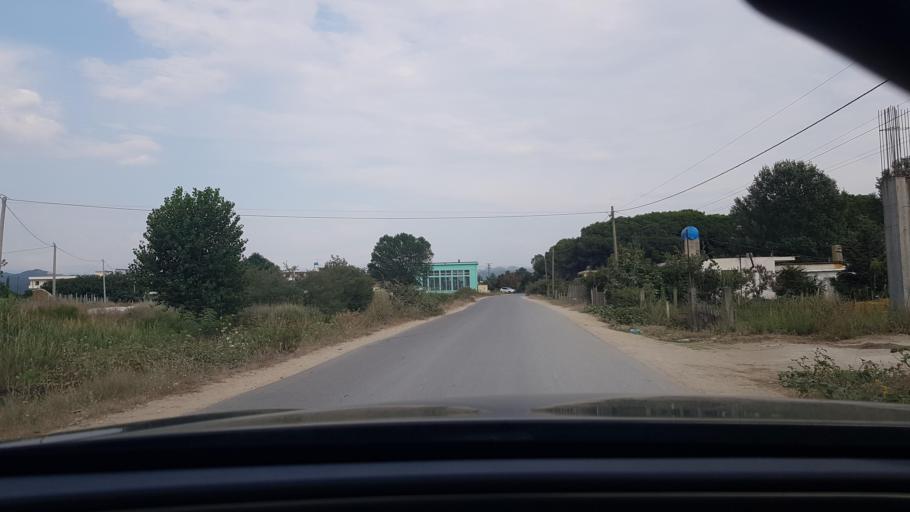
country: AL
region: Durres
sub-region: Rrethi i Durresit
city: Katundi i Ri
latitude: 41.4868
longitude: 19.5152
